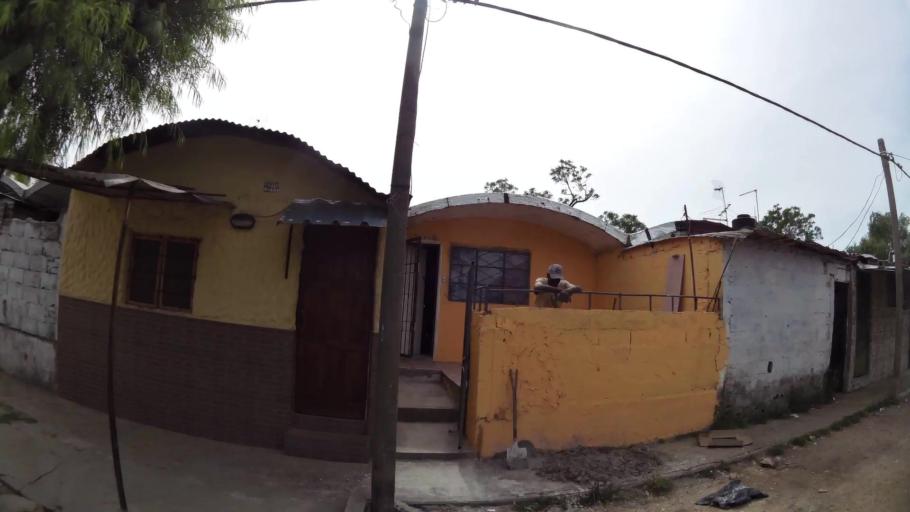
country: UY
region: Montevideo
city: Montevideo
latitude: -34.8353
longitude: -56.1790
